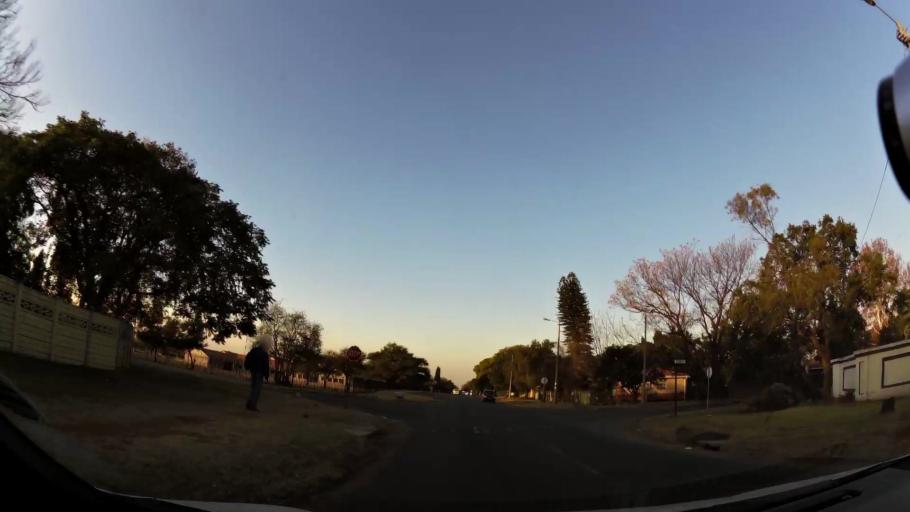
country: ZA
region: North-West
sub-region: Bojanala Platinum District Municipality
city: Rustenburg
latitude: -25.6757
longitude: 27.2226
